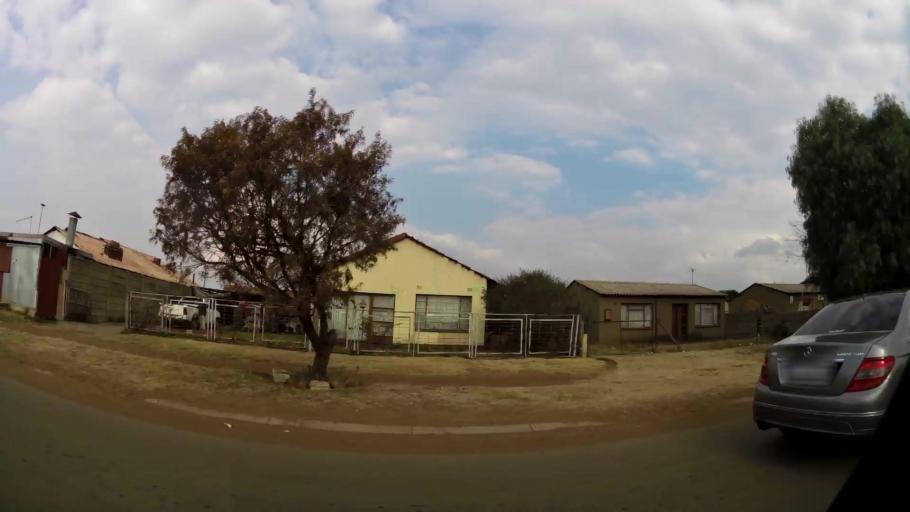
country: ZA
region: Gauteng
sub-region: Sedibeng District Municipality
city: Vanderbijlpark
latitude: -26.6812
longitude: 27.8702
